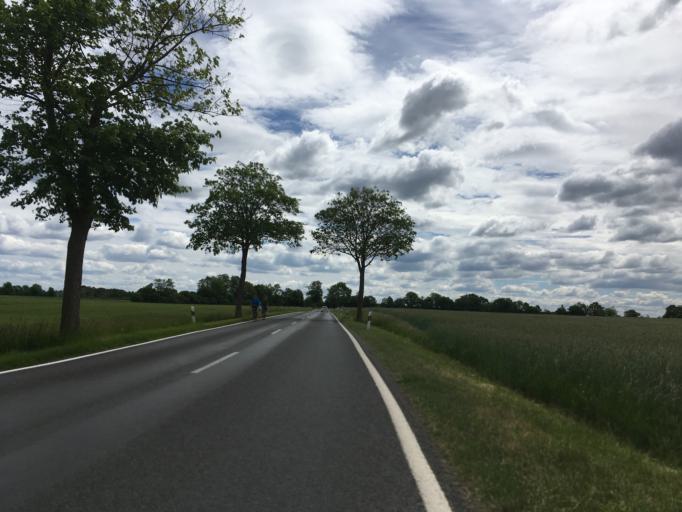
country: DE
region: Brandenburg
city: Melchow
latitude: 52.7456
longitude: 13.6940
